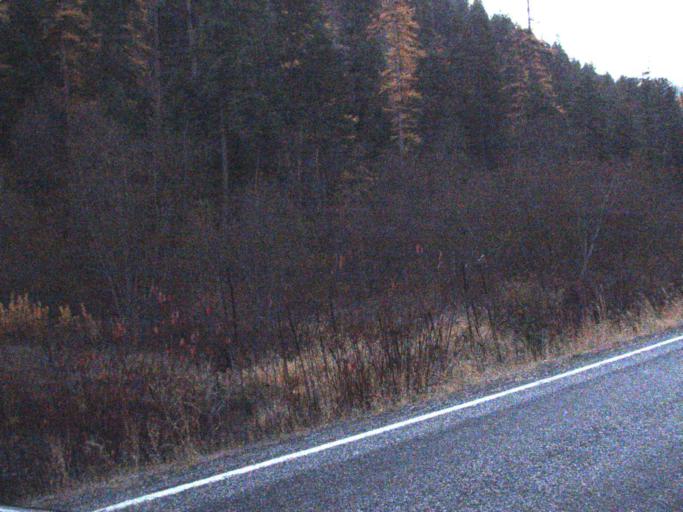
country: US
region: Washington
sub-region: Ferry County
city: Republic
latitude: 48.4892
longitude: -118.7388
